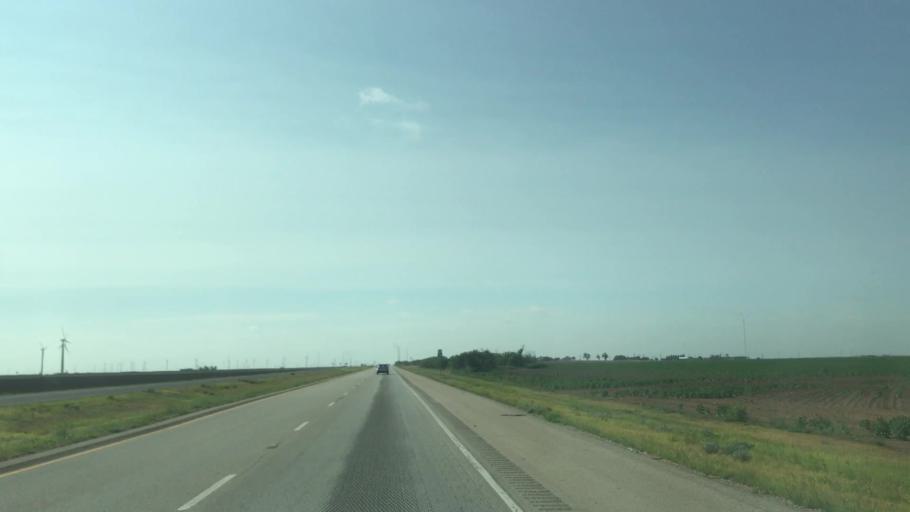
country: US
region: Texas
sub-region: Scurry County
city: Snyder
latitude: 32.6269
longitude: -100.7588
